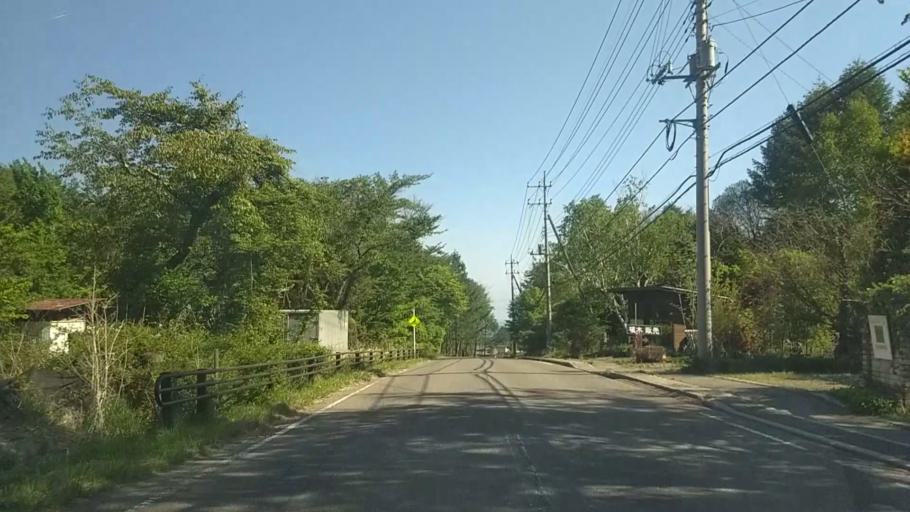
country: JP
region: Yamanashi
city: Nirasaki
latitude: 35.9019
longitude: 138.4094
